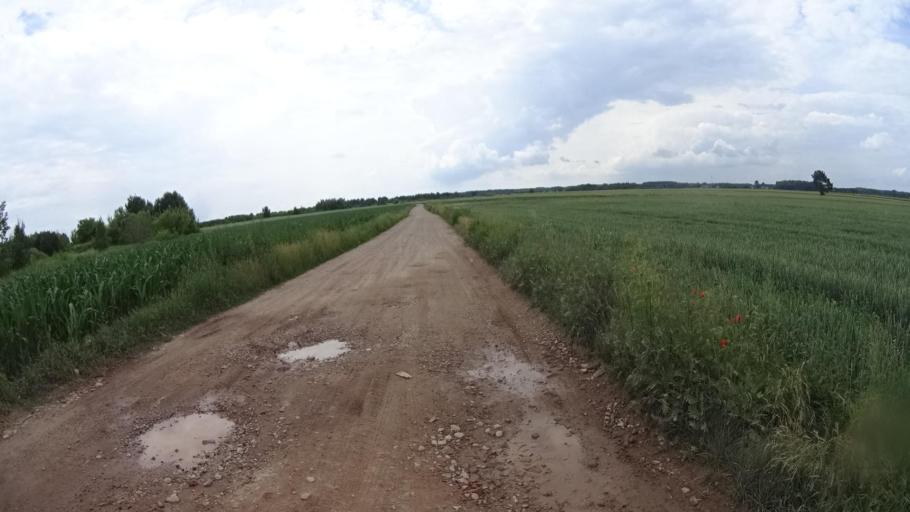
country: PL
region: Masovian Voivodeship
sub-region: Powiat piaseczynski
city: Tarczyn
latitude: 52.0281
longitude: 20.8193
